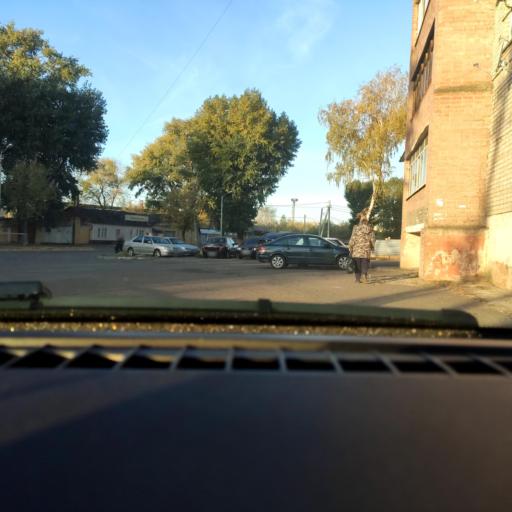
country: RU
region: Voronezj
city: Maslovka
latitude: 51.5988
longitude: 39.2562
